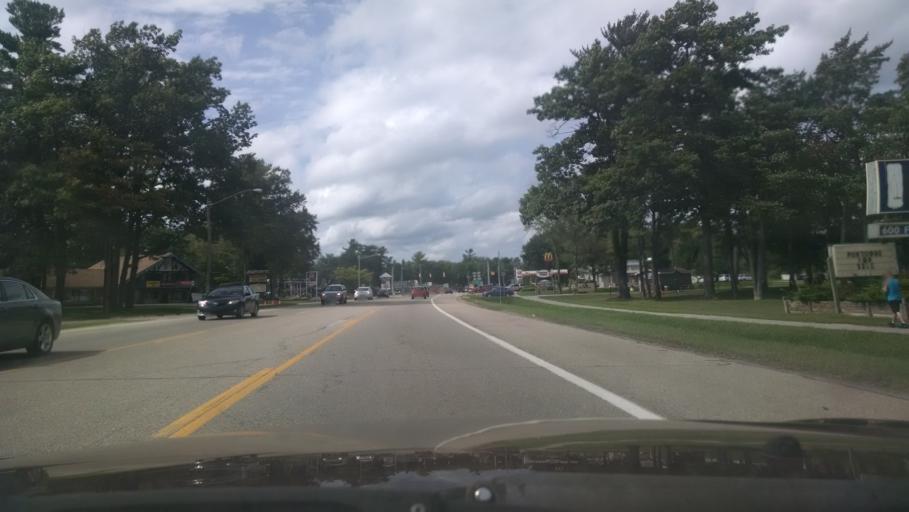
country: US
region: Michigan
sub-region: Wexford County
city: Cadillac
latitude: 44.2341
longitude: -85.4511
